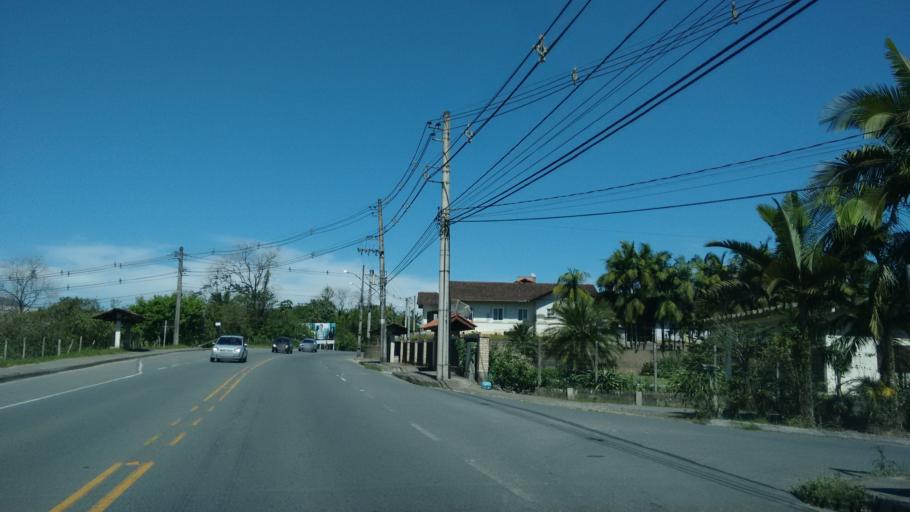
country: BR
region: Santa Catarina
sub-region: Pomerode
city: Pomerode
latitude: -26.7566
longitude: -49.1719
